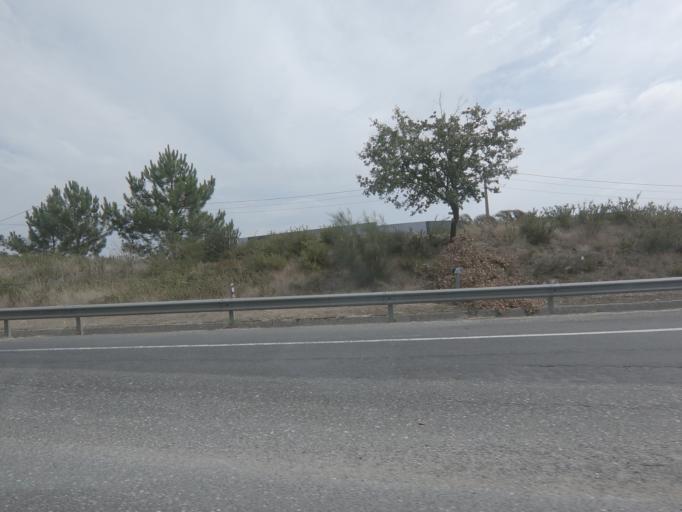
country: PT
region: Leiria
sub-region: Leiria
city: Leiria
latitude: 39.7668
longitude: -8.7765
